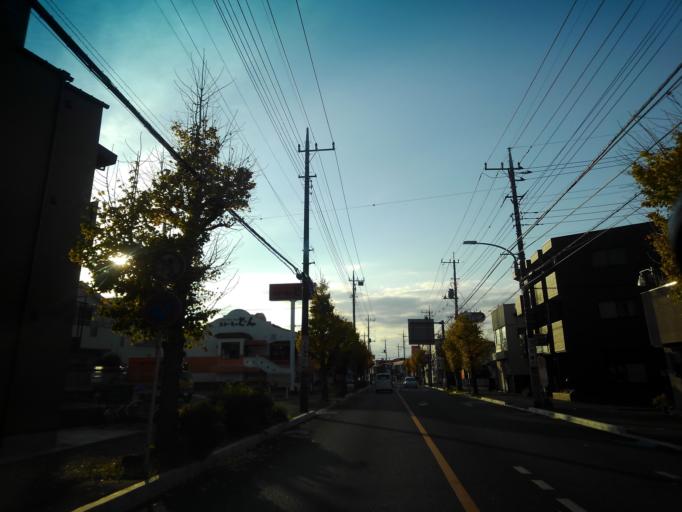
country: JP
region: Saitama
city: Tokorozawa
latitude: 35.7886
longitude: 139.4608
